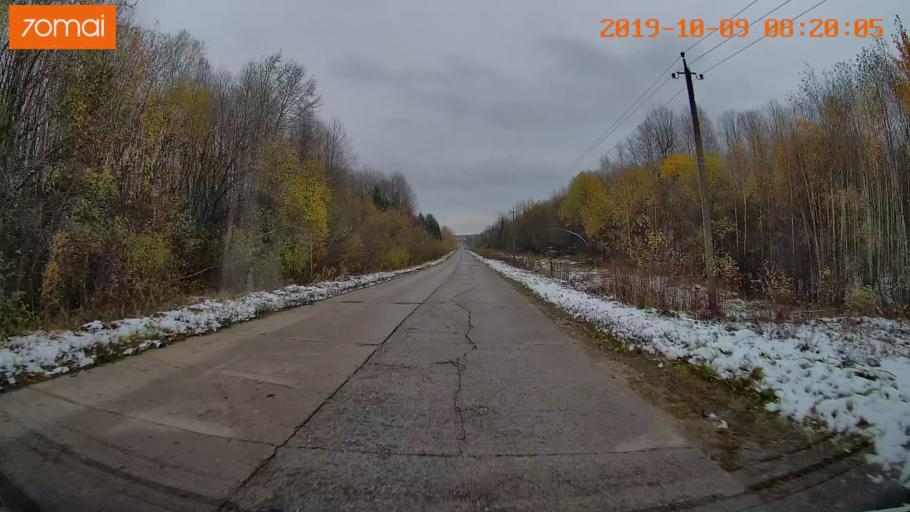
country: RU
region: Vologda
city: Gryazovets
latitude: 58.7430
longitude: 40.2537
